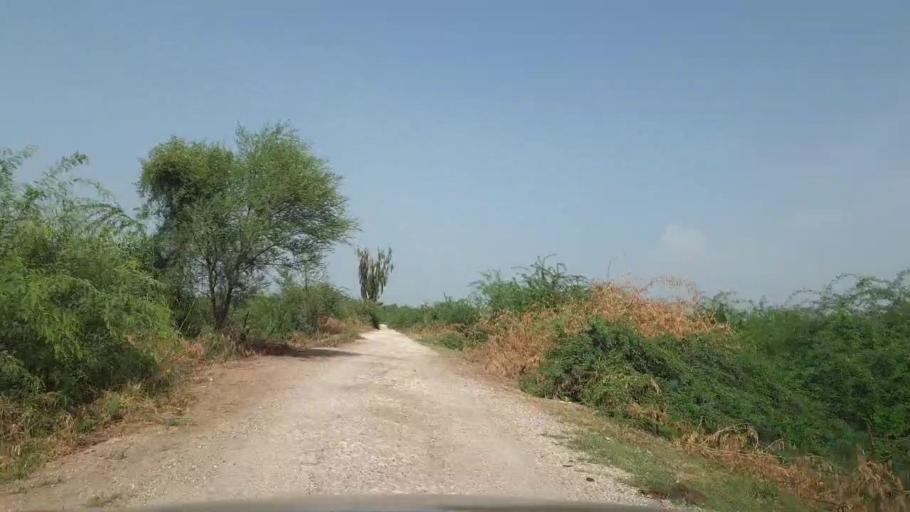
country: PK
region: Sindh
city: Pano Aqil
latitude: 27.7556
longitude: 69.1771
